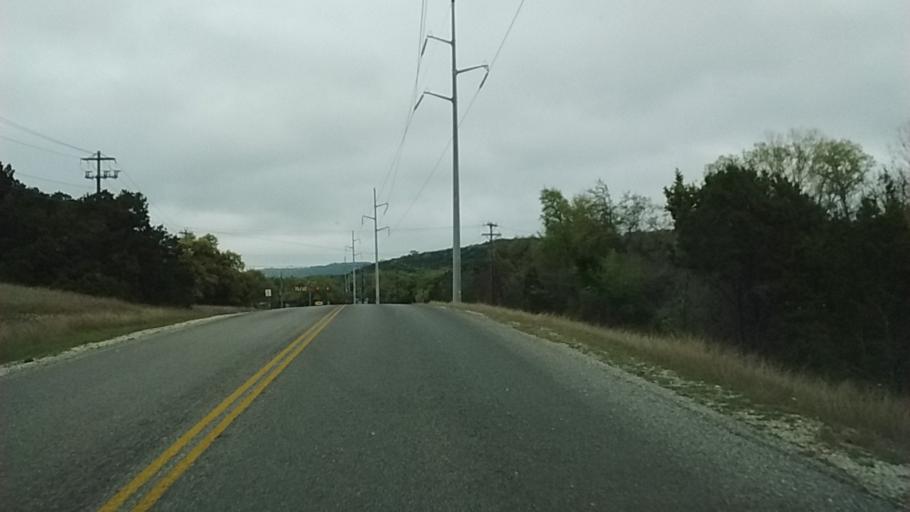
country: US
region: Texas
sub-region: Comal County
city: Canyon Lake
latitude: 29.8744
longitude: -98.1951
